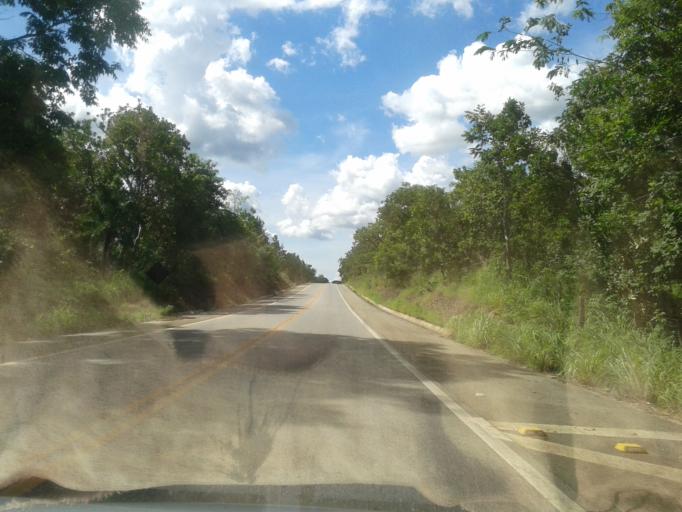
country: BR
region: Goias
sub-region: Itapuranga
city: Itapuranga
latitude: -15.5560
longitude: -50.2845
